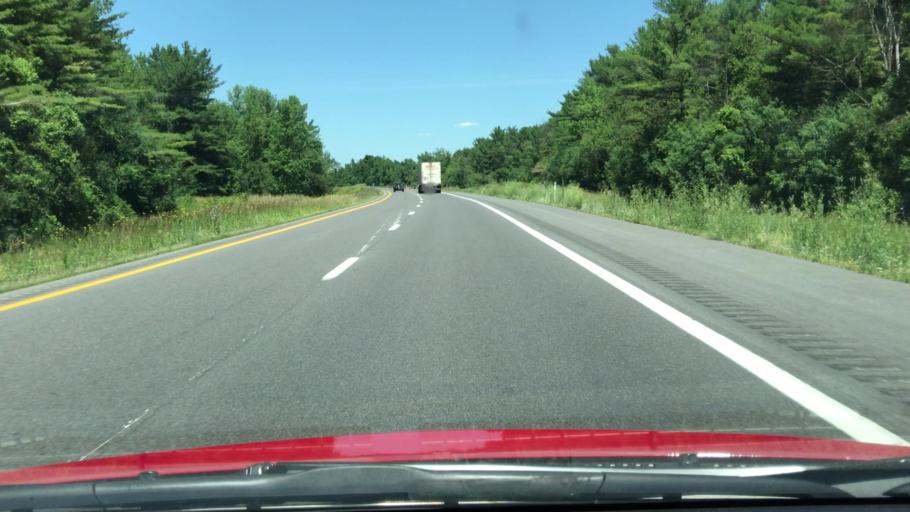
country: US
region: New York
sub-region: Clinton County
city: Cumberland Head
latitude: 44.7487
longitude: -73.4272
